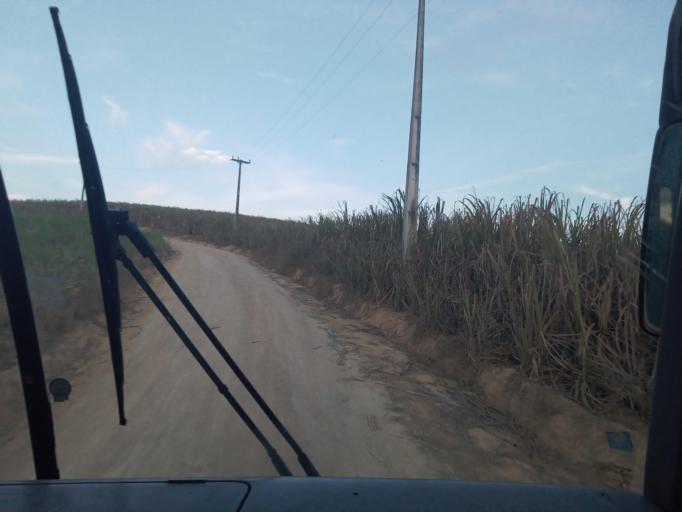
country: BR
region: Pernambuco
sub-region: Vitoria De Santo Antao
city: Vitoria de Santo Antao
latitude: -8.1617
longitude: -35.2591
